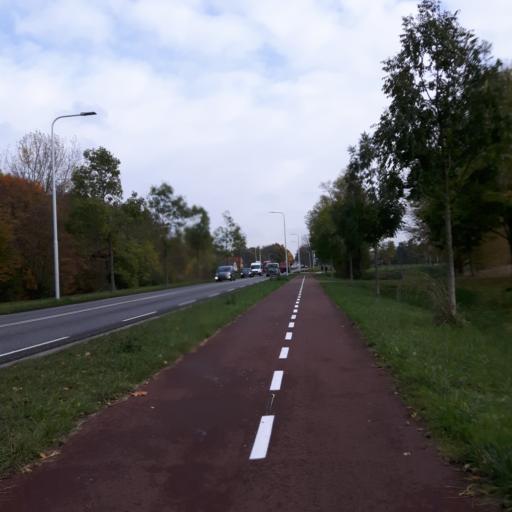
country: NL
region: Zeeland
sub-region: Gemeente Goes
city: Goes
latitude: 51.5090
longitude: 3.8817
